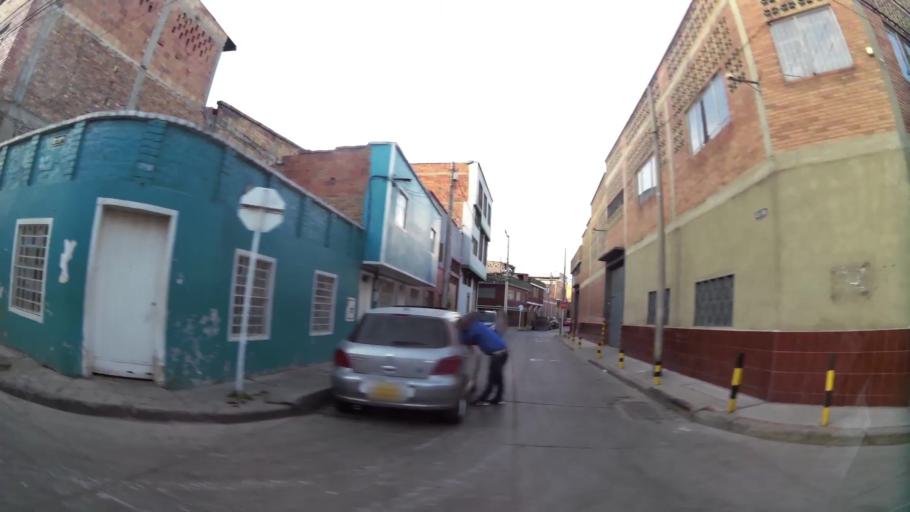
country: CO
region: Bogota D.C.
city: Bogota
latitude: 4.5622
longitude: -74.1333
